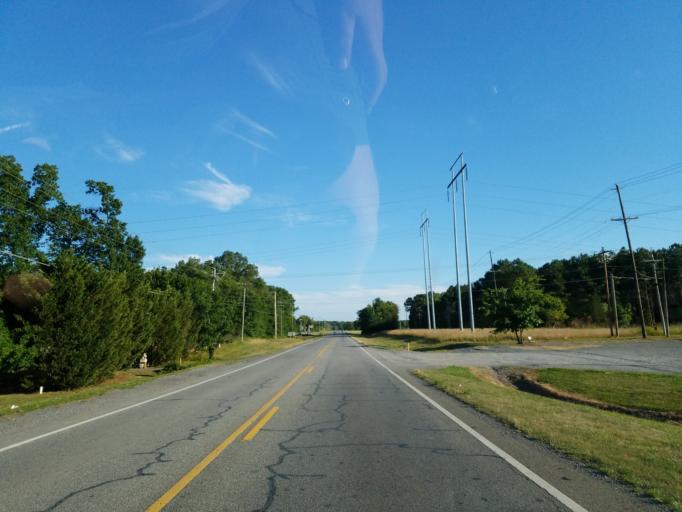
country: US
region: Georgia
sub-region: Gordon County
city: Calhoun
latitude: 34.4700
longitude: -84.9345
